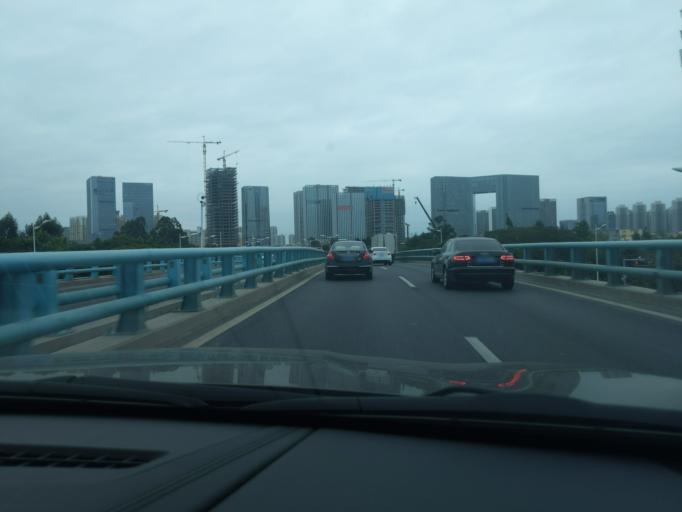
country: CN
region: Fujian
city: Liuwudian
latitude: 24.5190
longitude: 118.1762
